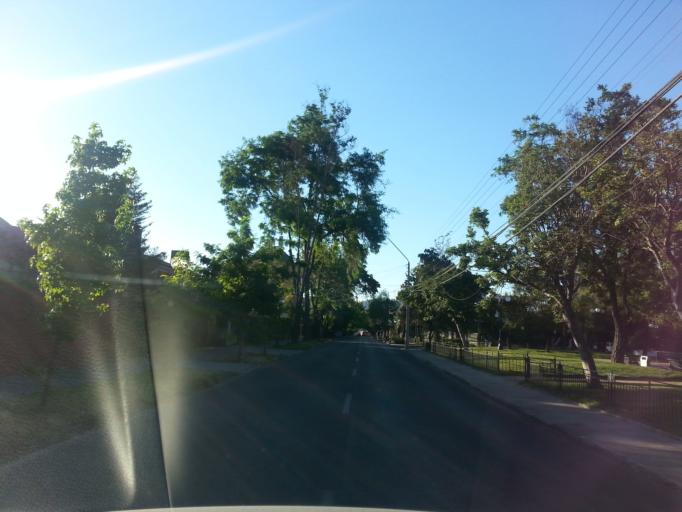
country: CL
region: Santiago Metropolitan
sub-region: Provincia de Santiago
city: Villa Presidente Frei, Nunoa, Santiago, Chile
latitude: -33.4444
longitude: -70.5905
